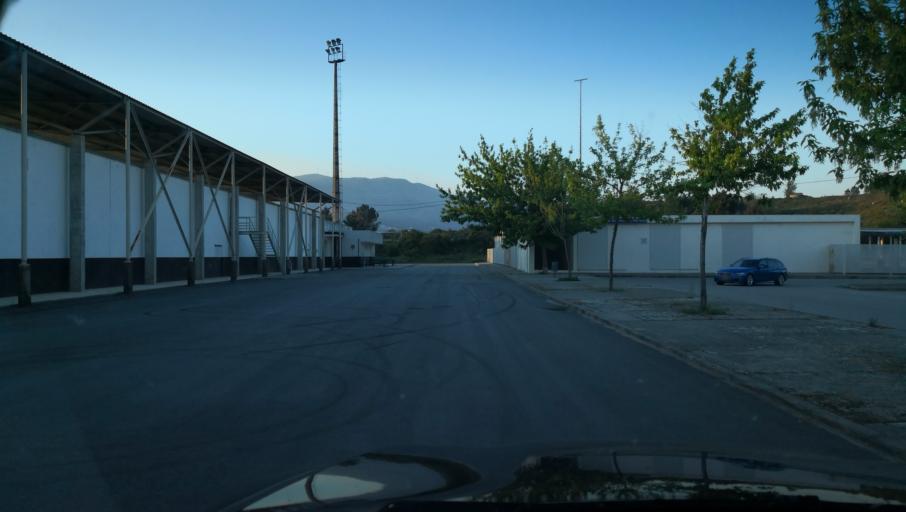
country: PT
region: Vila Real
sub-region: Vila Real
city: Vila Real
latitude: 41.2872
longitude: -7.7550
